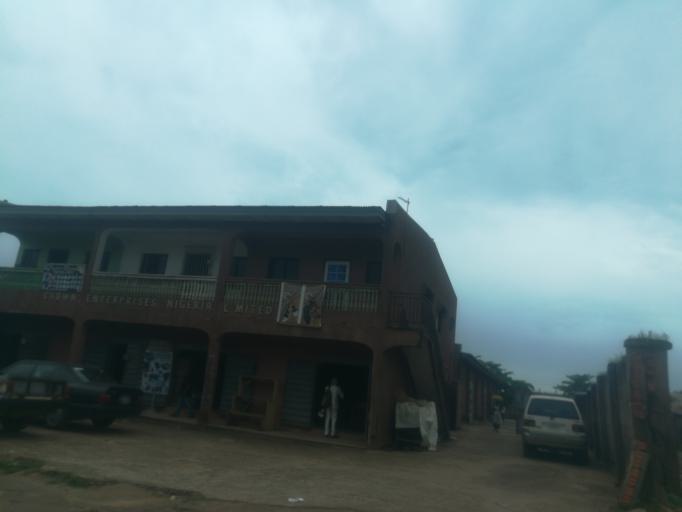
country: NG
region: Oyo
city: Ibadan
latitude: 7.3896
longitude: 3.9506
